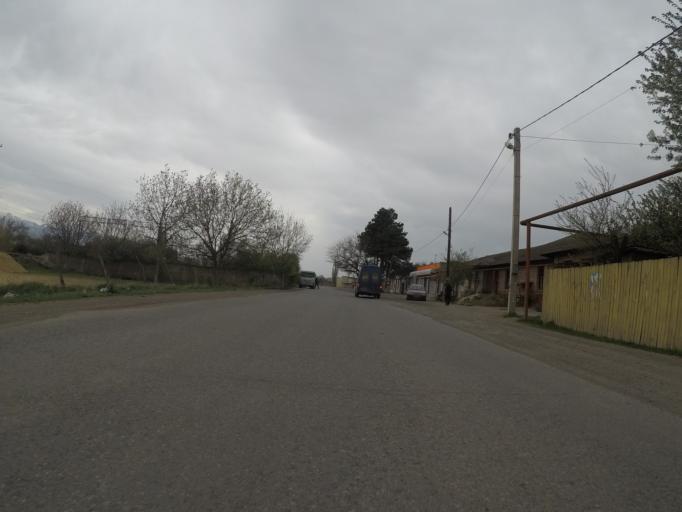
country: GE
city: Agara
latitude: 42.0212
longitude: 43.7300
